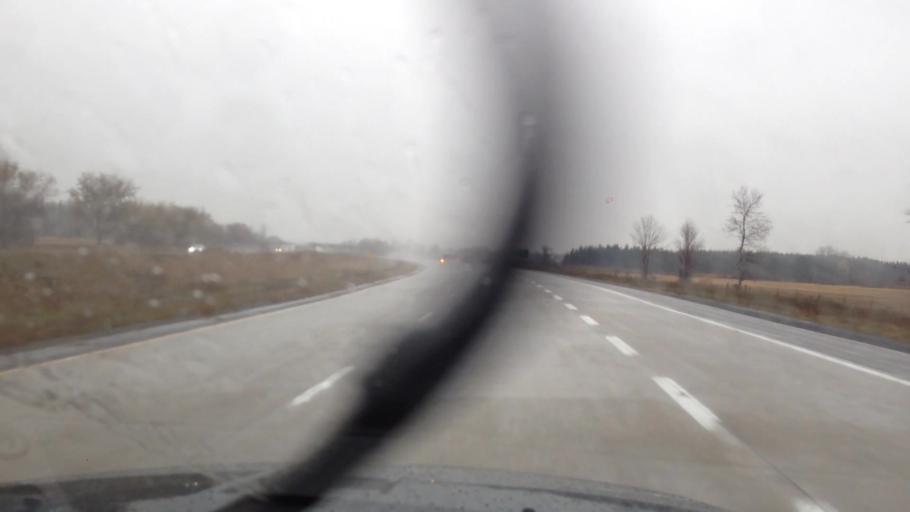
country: CA
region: Ontario
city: Hawkesbury
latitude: 45.5114
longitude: -74.5684
